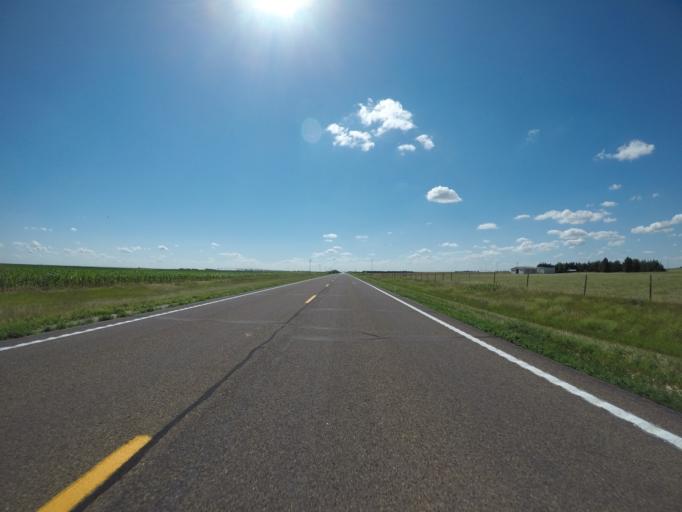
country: US
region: Nebraska
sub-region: Chase County
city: Imperial
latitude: 40.5377
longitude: -101.8730
